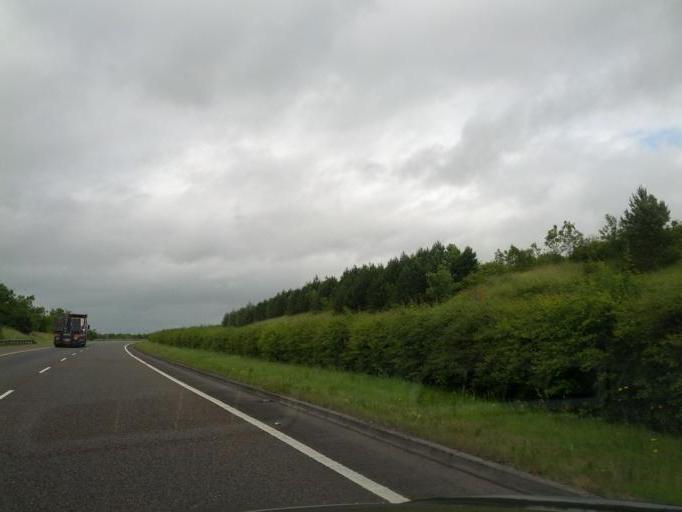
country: IE
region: Munster
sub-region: An Clar
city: Newmarket on Fergus
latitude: 52.7750
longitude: -8.9192
